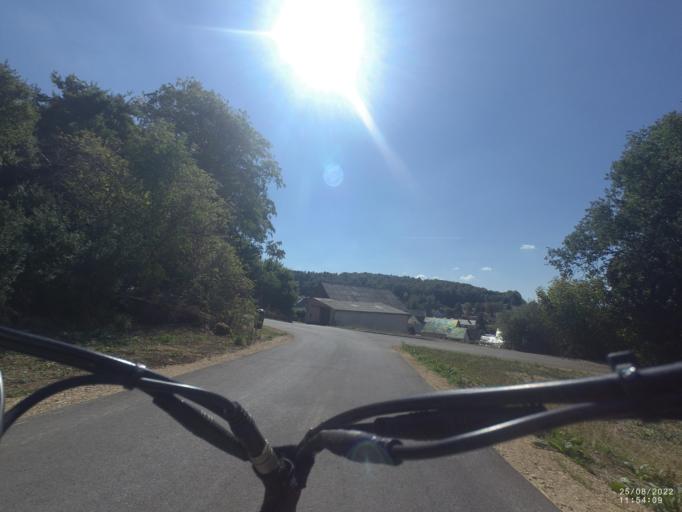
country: DE
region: Rheinland-Pfalz
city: Berlingen
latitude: 50.2412
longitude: 6.7170
